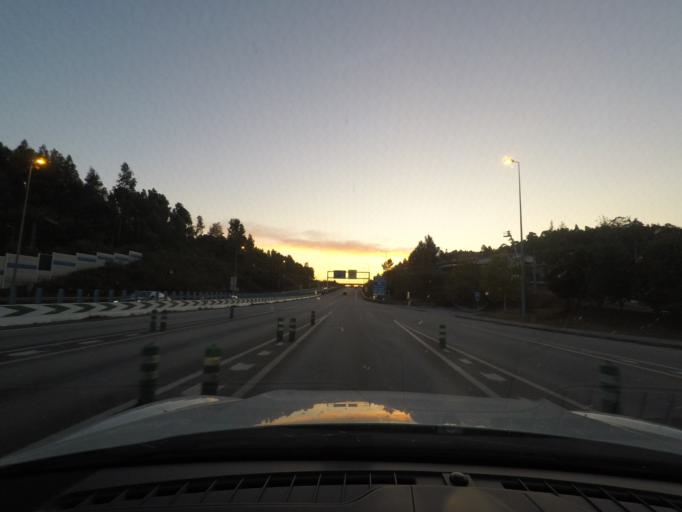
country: PT
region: Porto
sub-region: Lousada
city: Lousada
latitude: 41.2925
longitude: -8.2698
